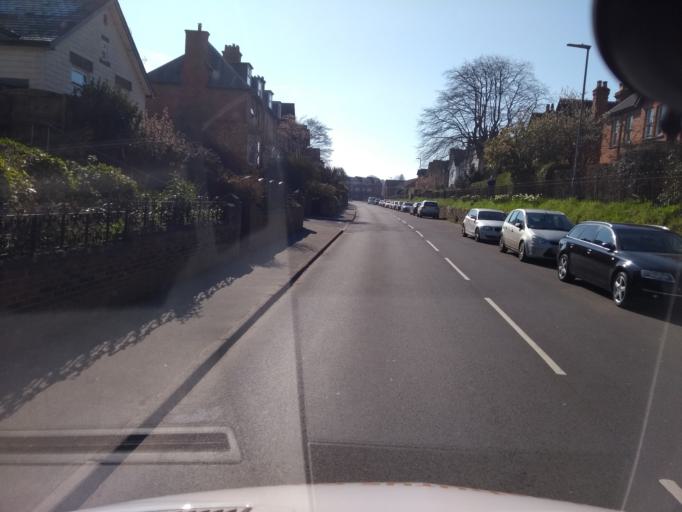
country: GB
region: England
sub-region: Somerset
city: Bishops Lydeard
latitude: 50.9825
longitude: -3.2385
